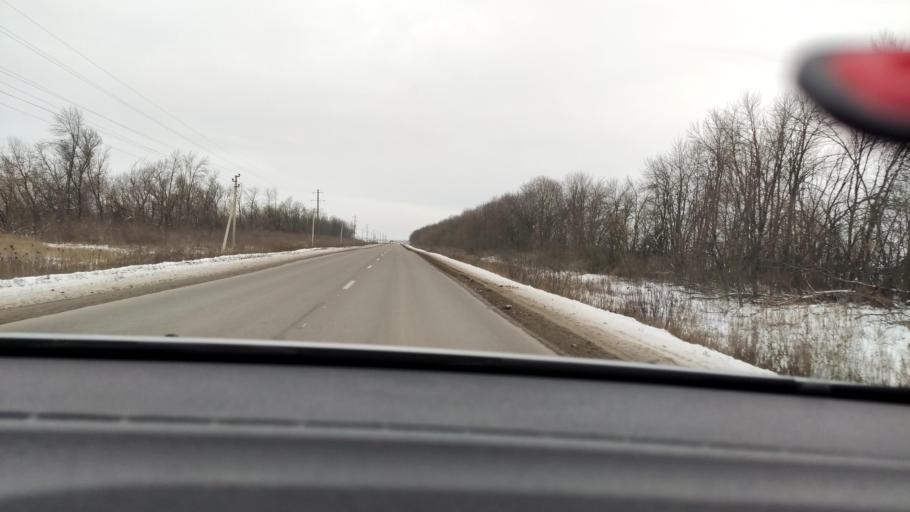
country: RU
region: Voronezj
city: Latnaya
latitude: 51.7575
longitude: 38.9191
